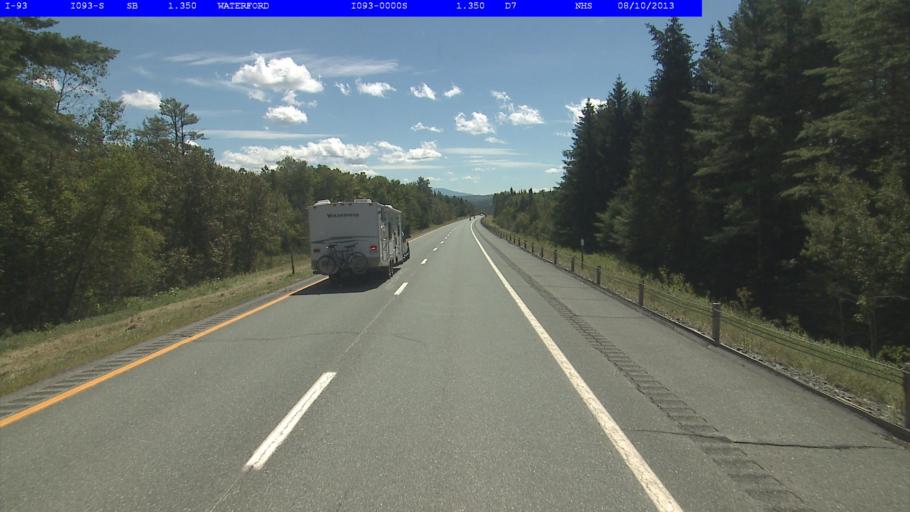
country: US
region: Vermont
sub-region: Caledonia County
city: Saint Johnsbury
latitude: 44.3617
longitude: -71.9002
